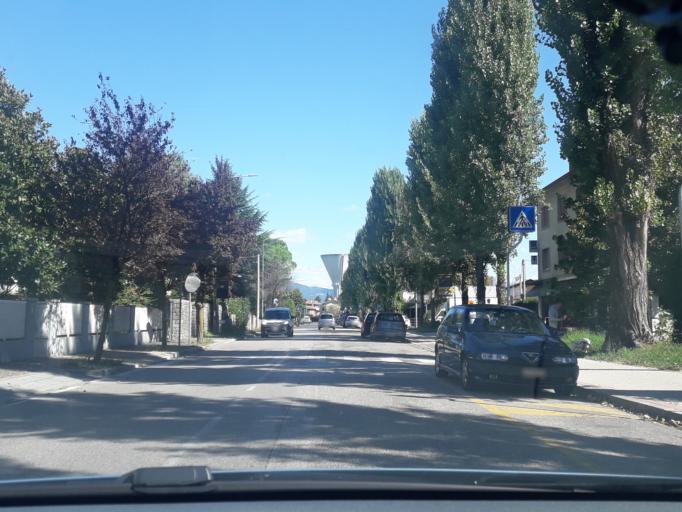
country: IT
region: Friuli Venezia Giulia
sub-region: Provincia di Udine
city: Udine
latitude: 46.0734
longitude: 13.2452
